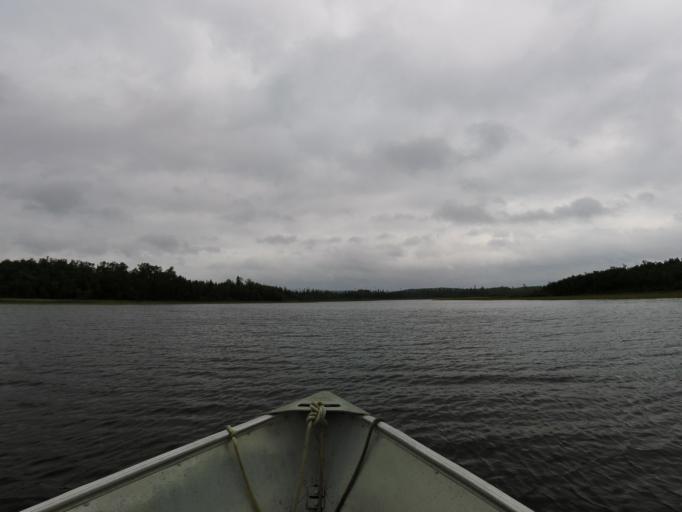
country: CA
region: Ontario
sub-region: Rainy River District
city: Atikokan
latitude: 49.5978
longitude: -91.3516
